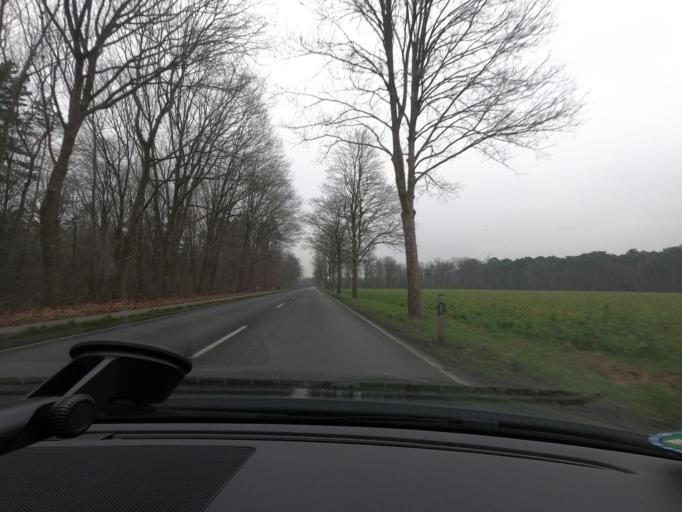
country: DE
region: North Rhine-Westphalia
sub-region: Regierungsbezirk Dusseldorf
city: Nettetal
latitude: 51.3700
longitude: 6.2471
